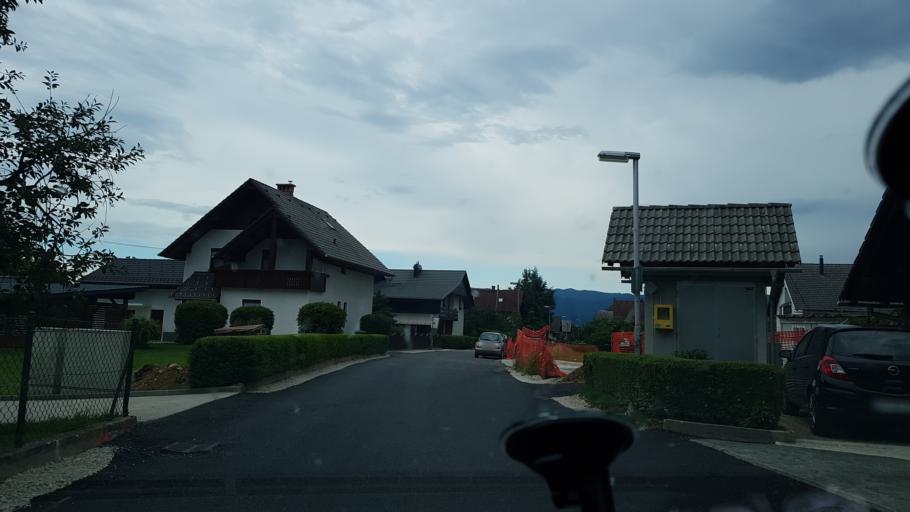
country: SI
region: Zirovnica
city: Zirovnica
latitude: 46.3978
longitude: 14.1273
